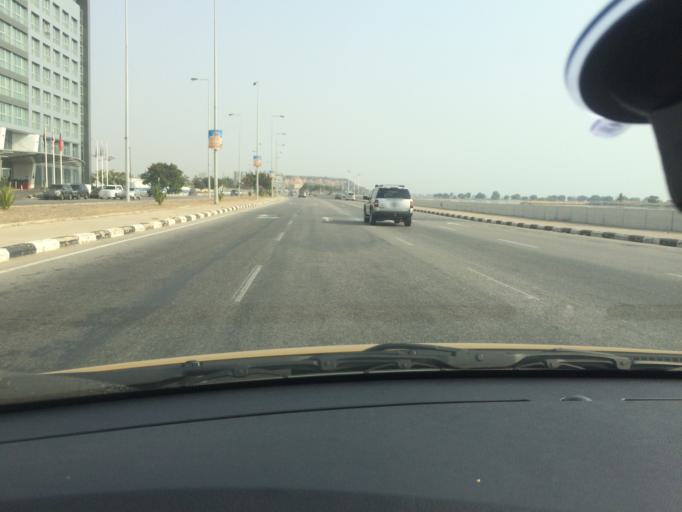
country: AO
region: Luanda
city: Luanda
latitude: -8.8186
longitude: 13.2168
